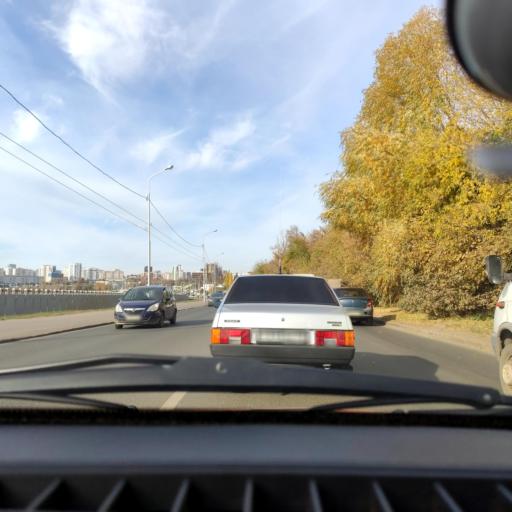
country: RU
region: Bashkortostan
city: Ufa
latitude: 54.7045
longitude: 55.9674
